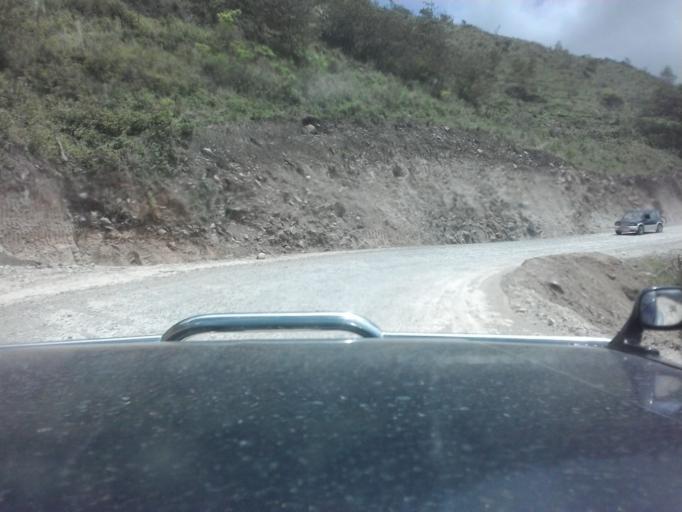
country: CR
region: Guanacaste
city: Juntas
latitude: 10.2696
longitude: -84.8367
